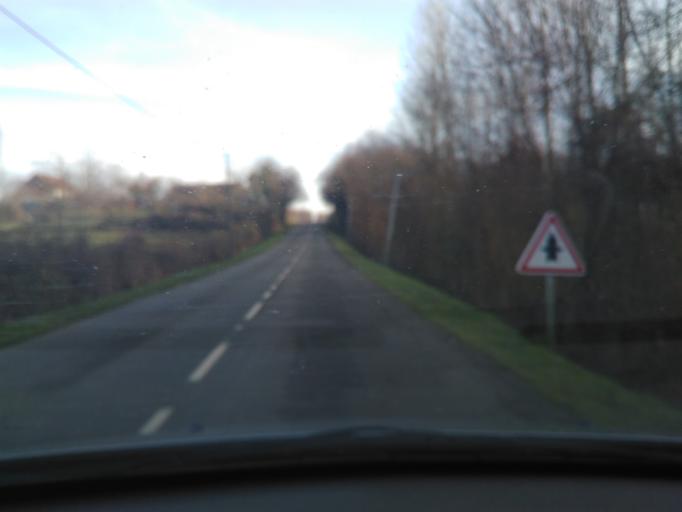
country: FR
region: Bourgogne
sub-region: Departement de la Nievre
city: Dornes
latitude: 46.7721
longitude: 3.3056
